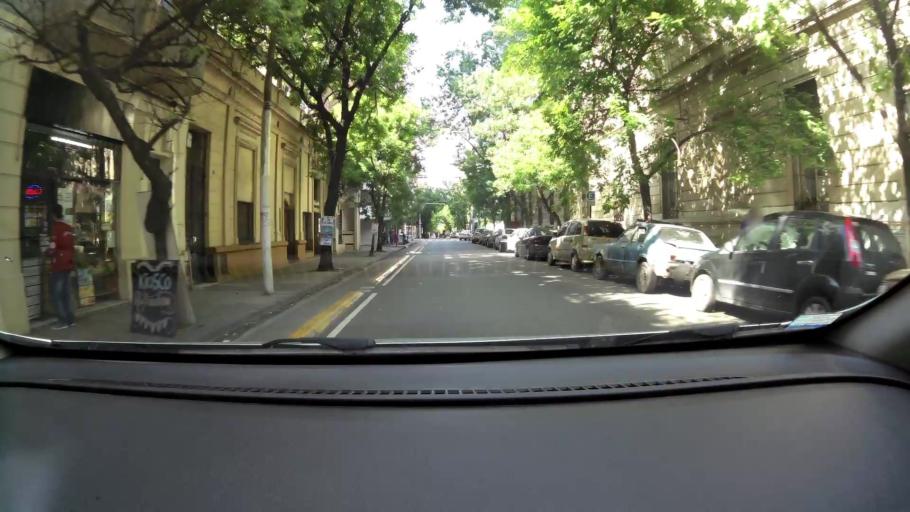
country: AR
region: Santa Fe
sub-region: Departamento de Rosario
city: Rosario
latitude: -32.9564
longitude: -60.6304
